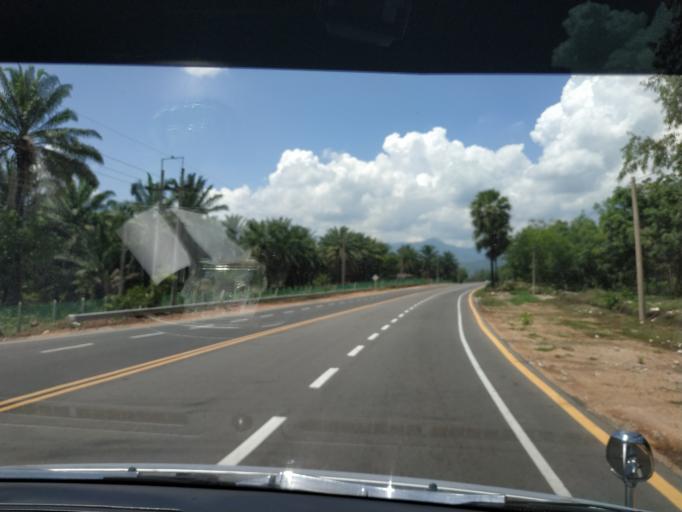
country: MM
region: Mon
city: Kyaikto
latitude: 17.3707
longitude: 97.0496
